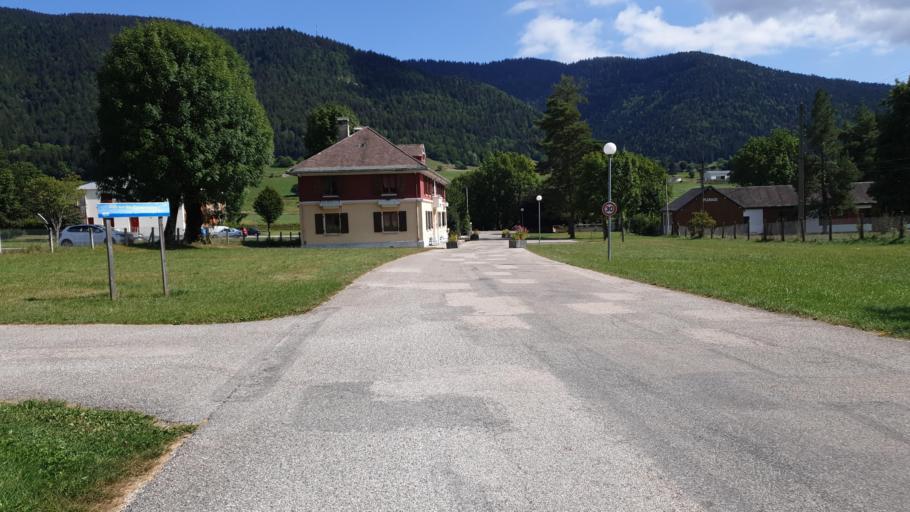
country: FR
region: Rhone-Alpes
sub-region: Departement de l'Isere
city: Autrans
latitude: 45.1812
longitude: 5.5537
